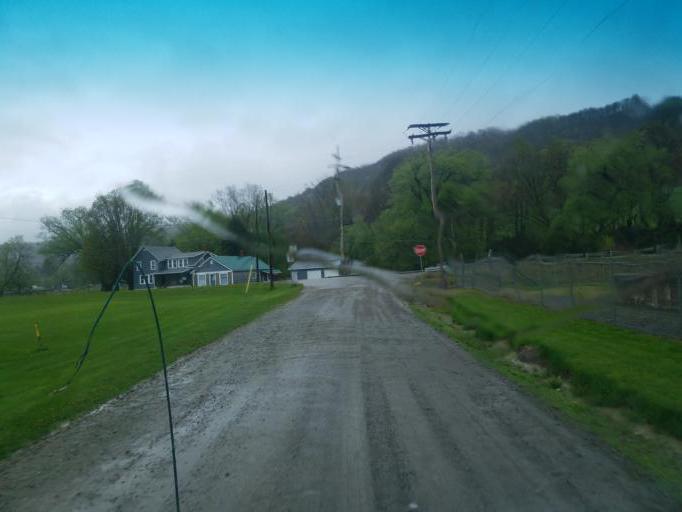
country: US
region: Pennsylvania
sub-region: Tioga County
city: Westfield
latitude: 41.9192
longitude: -77.6234
